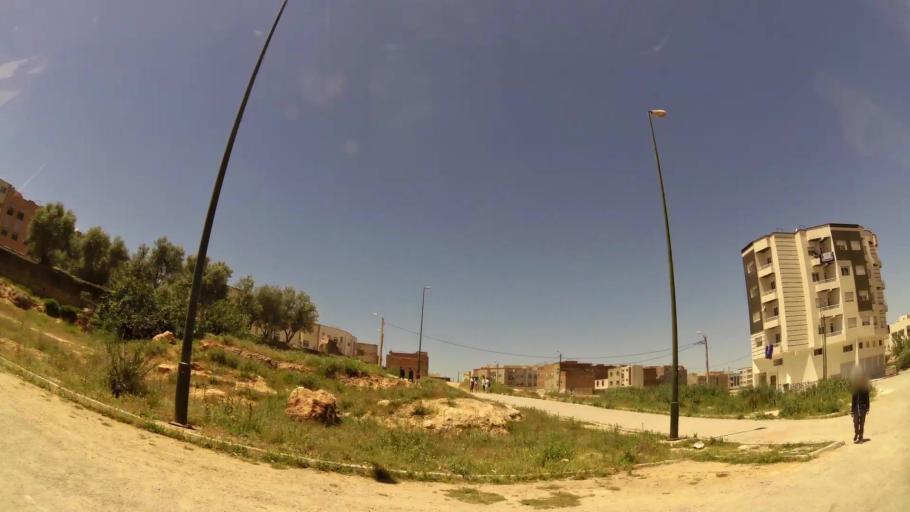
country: MA
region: Meknes-Tafilalet
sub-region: Meknes
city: Meknes
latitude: 33.8557
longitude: -5.5568
